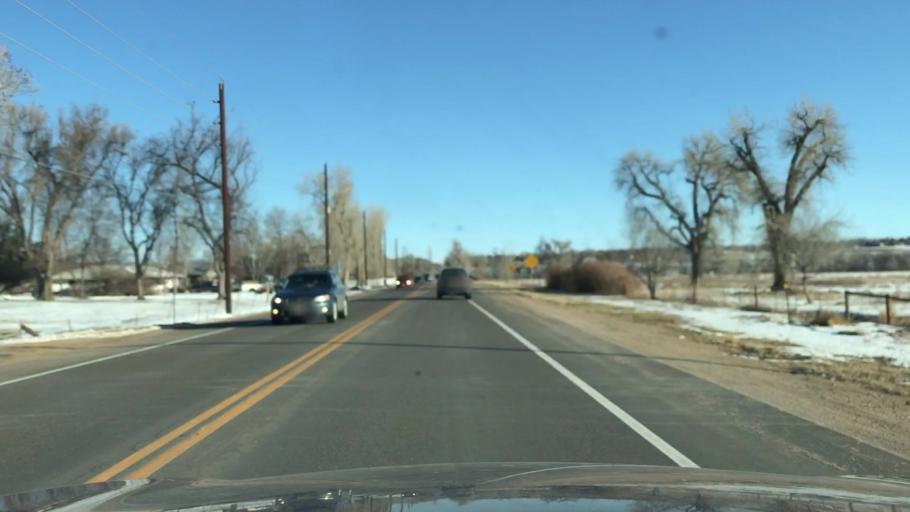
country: US
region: Colorado
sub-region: Boulder County
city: Gunbarrel
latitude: 40.0429
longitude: -105.1784
